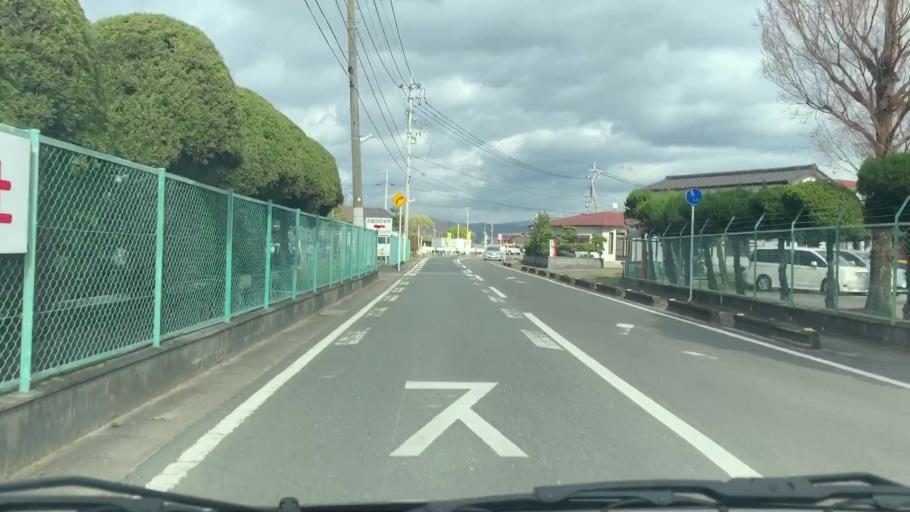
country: JP
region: Saga Prefecture
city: Saga-shi
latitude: 33.2545
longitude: 130.2280
